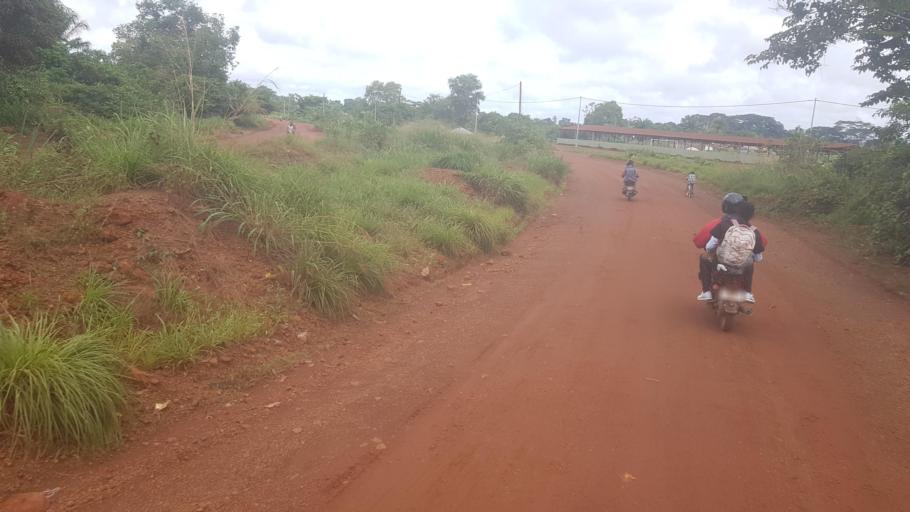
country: SL
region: Southern Province
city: Mogbwemo
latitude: 7.7658
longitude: -12.3012
